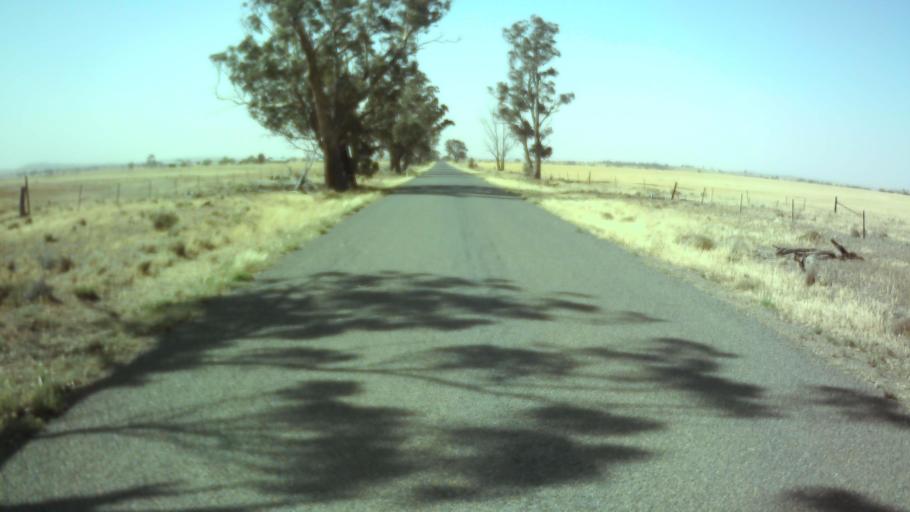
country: AU
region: New South Wales
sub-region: Weddin
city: Grenfell
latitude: -33.8867
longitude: 147.9233
